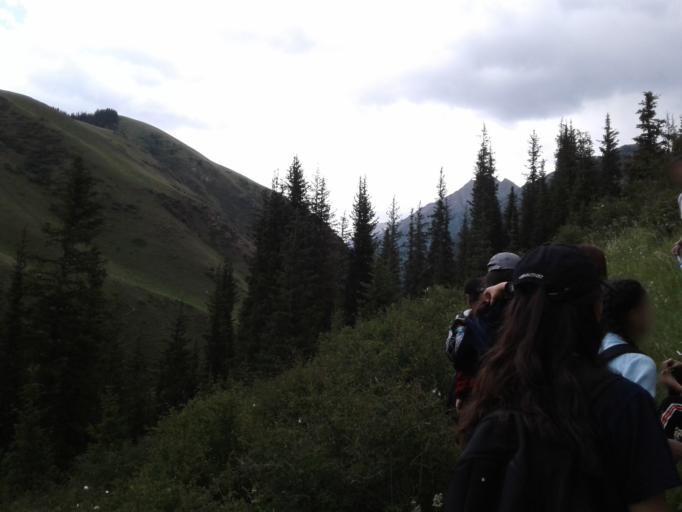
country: KG
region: Naryn
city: Naryn
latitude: 41.4539
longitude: 76.4533
